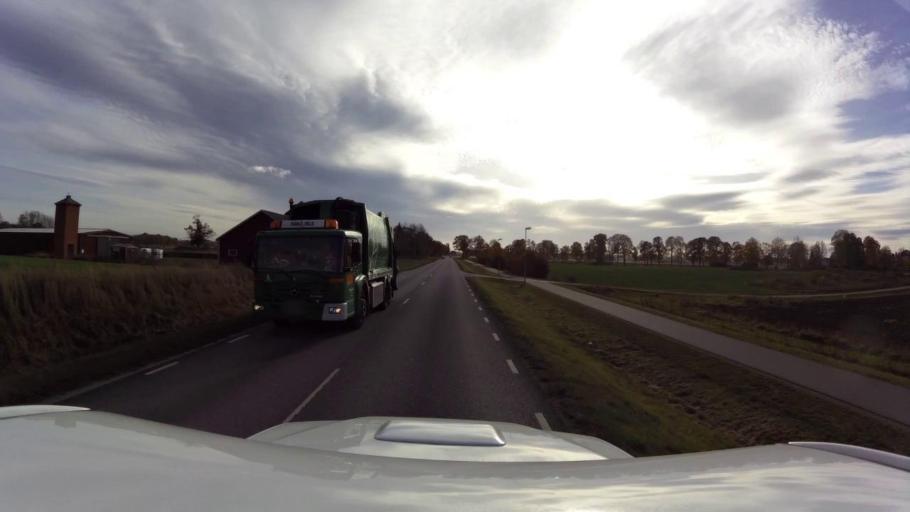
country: SE
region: OEstergoetland
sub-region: Linkopings Kommun
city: Ekangen
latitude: 58.4543
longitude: 15.6421
